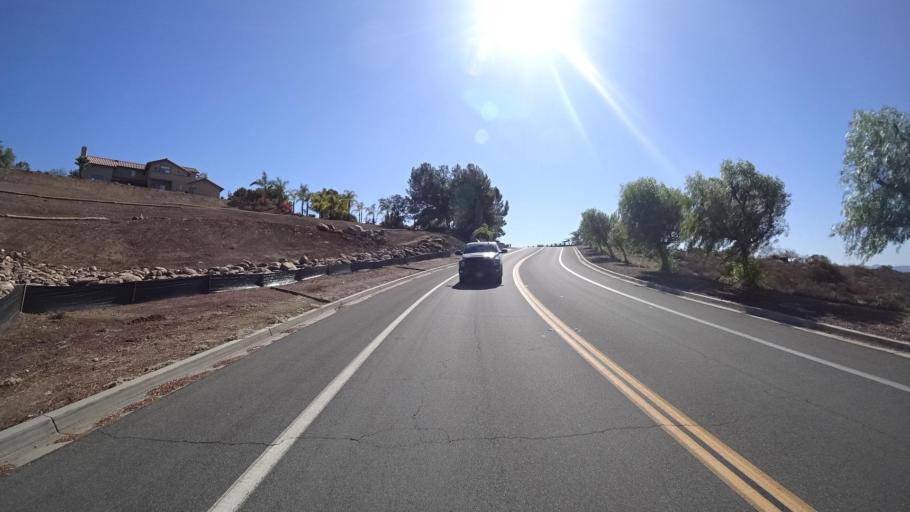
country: US
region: California
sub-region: San Diego County
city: Lakeside
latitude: 32.8573
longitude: -116.8754
